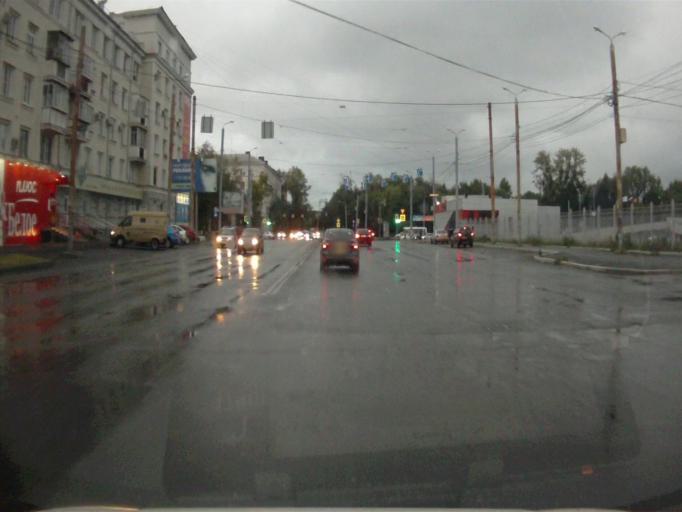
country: RU
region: Chelyabinsk
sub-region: Gorod Chelyabinsk
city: Chelyabinsk
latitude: 55.1624
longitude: 61.4339
